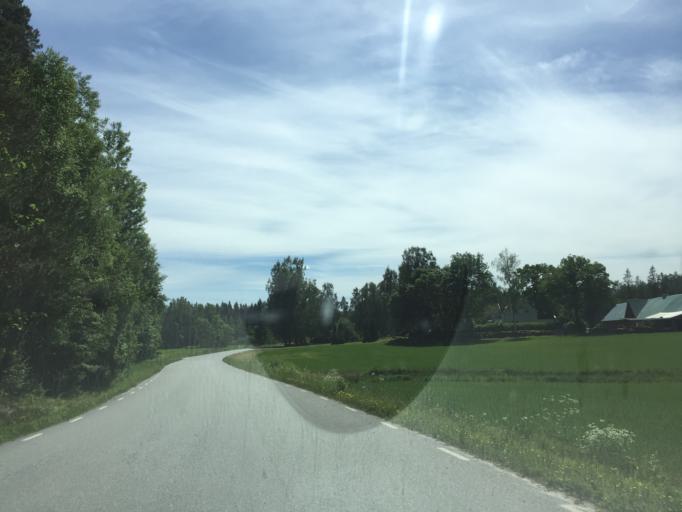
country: SE
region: OErebro
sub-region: Orebro Kommun
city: Hovsta
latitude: 59.3844
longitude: 15.1747
